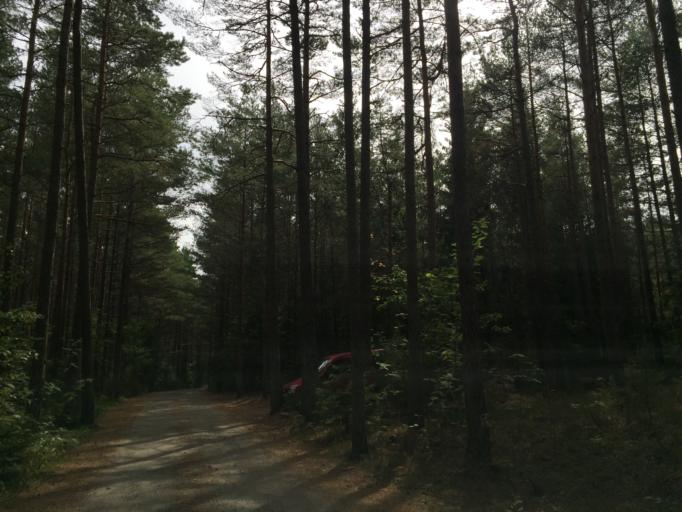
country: NO
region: Ostfold
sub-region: Hvaler
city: Skjaerhalden
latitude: 59.0305
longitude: 11.0251
